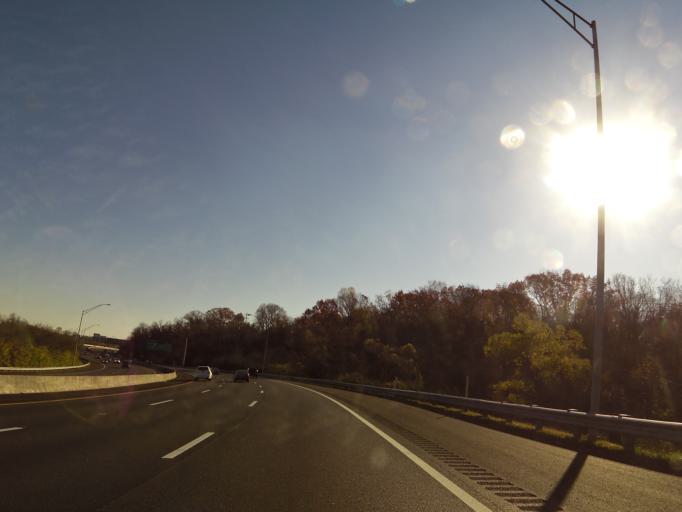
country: US
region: Tennessee
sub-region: Knox County
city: Knoxville
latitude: 35.9837
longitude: -83.9468
